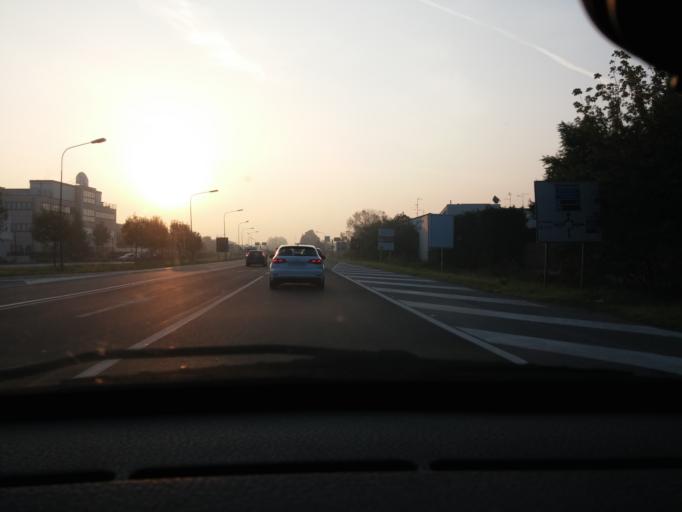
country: IT
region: Emilia-Romagna
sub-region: Provincia di Ferrara
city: Ferrara
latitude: 44.8200
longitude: 11.6004
